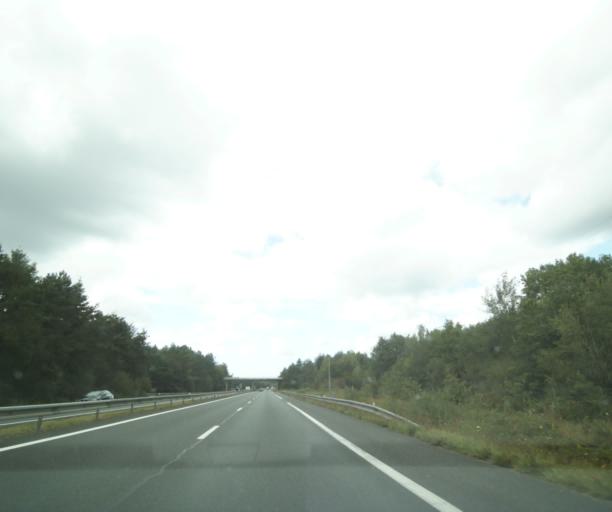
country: FR
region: Centre
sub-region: Departement du Loiret
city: La Ferte-Saint-Aubin
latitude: 47.6712
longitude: 1.9192
